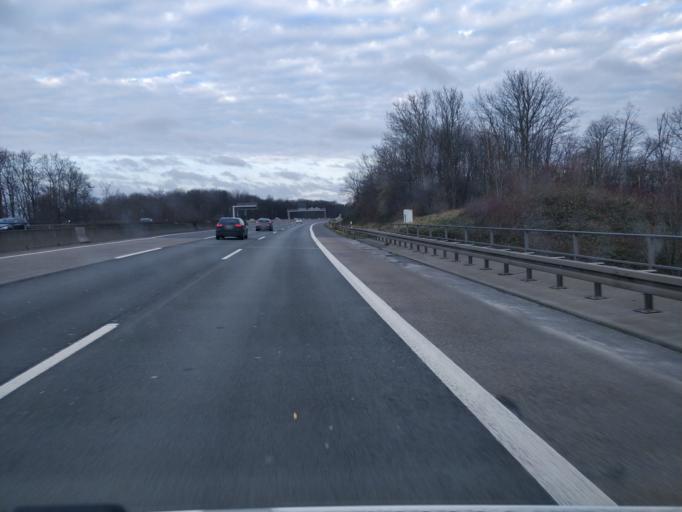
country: DE
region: North Rhine-Westphalia
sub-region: Regierungsbezirk Koln
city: Mengenich
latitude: 50.9778
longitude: 6.8512
